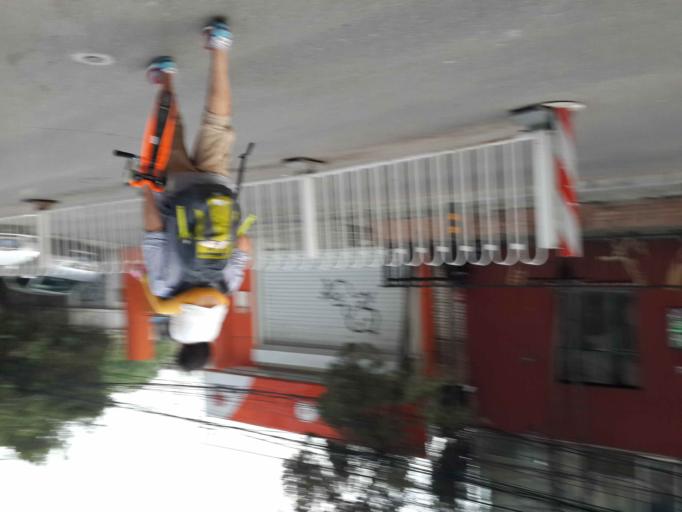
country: CN
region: Beijing
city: Chaowai
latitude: 39.9344
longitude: 116.4464
